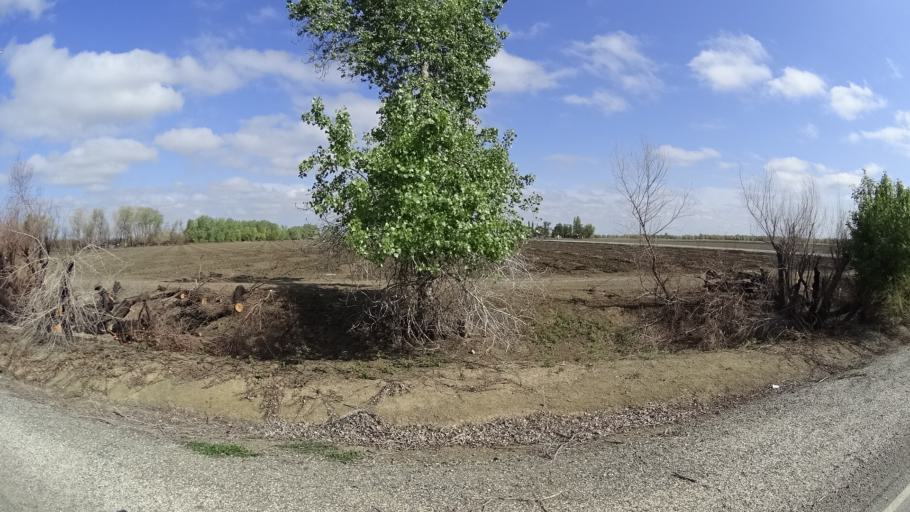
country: US
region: California
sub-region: Colusa County
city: Colusa
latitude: 39.3911
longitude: -121.9301
